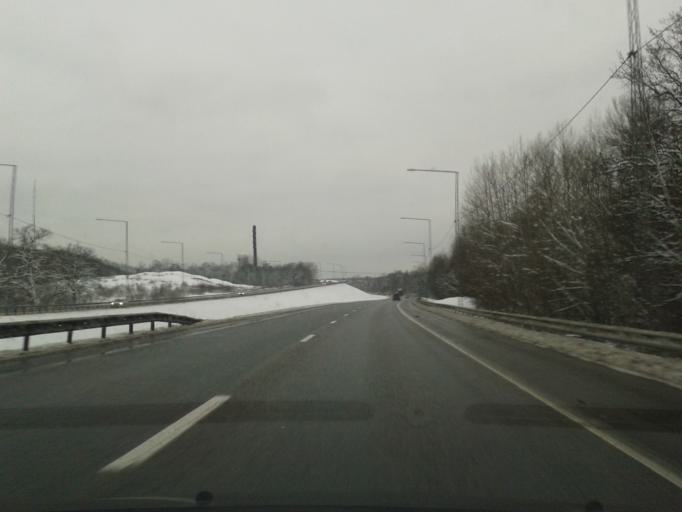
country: SE
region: Stockholm
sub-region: Nacka Kommun
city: Alta
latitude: 59.2618
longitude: 18.1559
